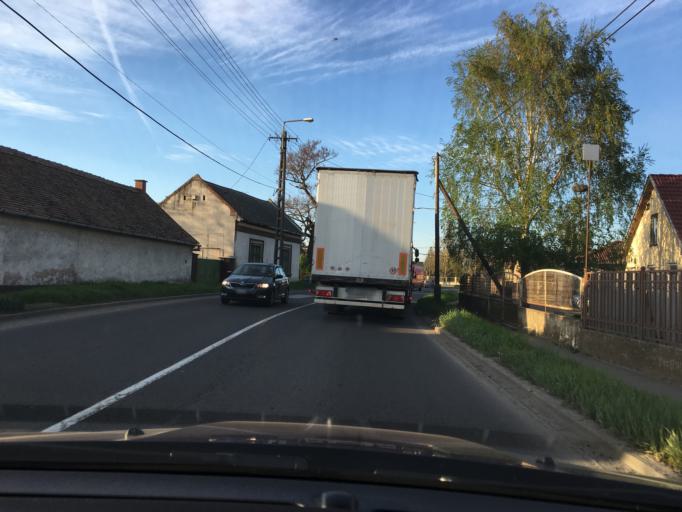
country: HU
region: Hajdu-Bihar
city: Mikepercs
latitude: 47.4414
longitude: 21.6318
